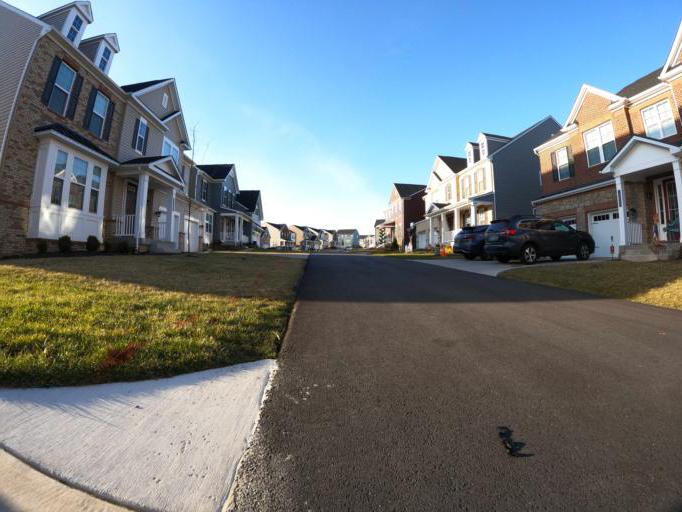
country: US
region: Maryland
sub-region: Howard County
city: Highland
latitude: 39.1955
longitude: -76.9393
